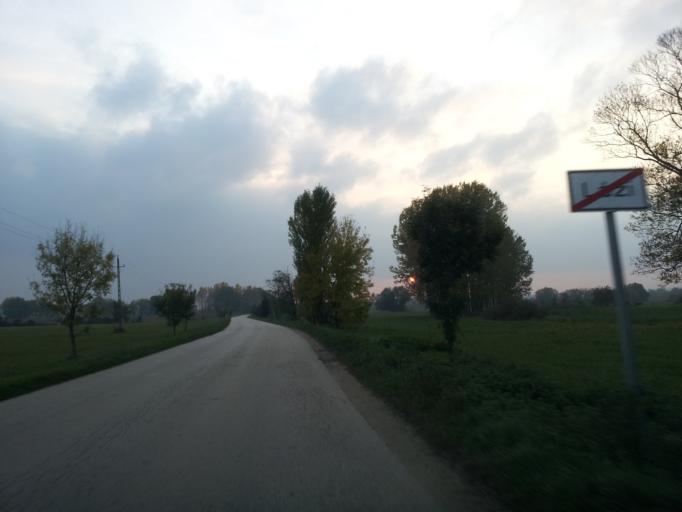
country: HU
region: Gyor-Moson-Sopron
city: Bakonyszentlaszlo
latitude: 47.4605
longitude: 17.8376
